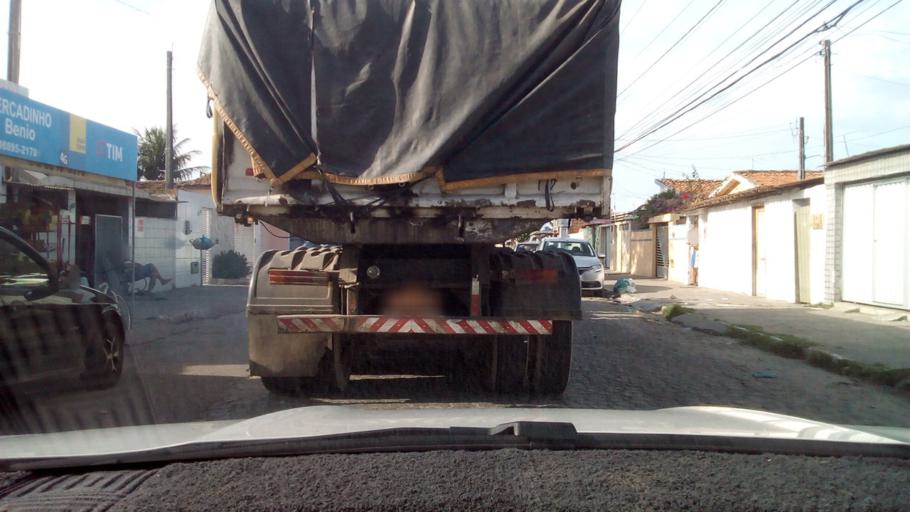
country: BR
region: Paraiba
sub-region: Cabedelo
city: Cabedelo
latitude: -6.9693
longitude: -34.8379
